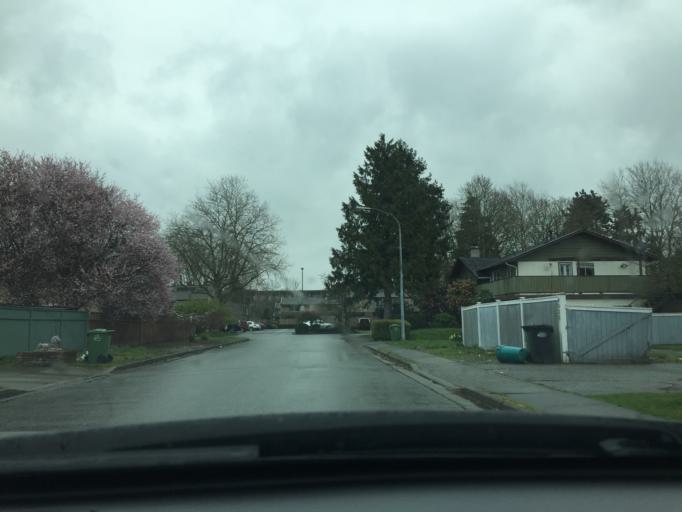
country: CA
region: British Columbia
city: Richmond
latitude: 49.1455
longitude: -123.1250
